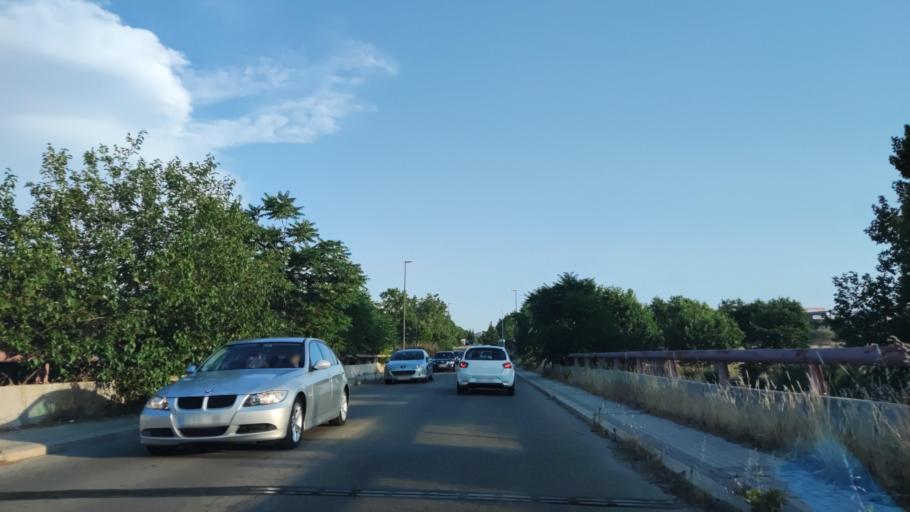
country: ES
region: Madrid
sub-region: Provincia de Madrid
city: Pinto
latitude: 40.2699
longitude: -3.6946
